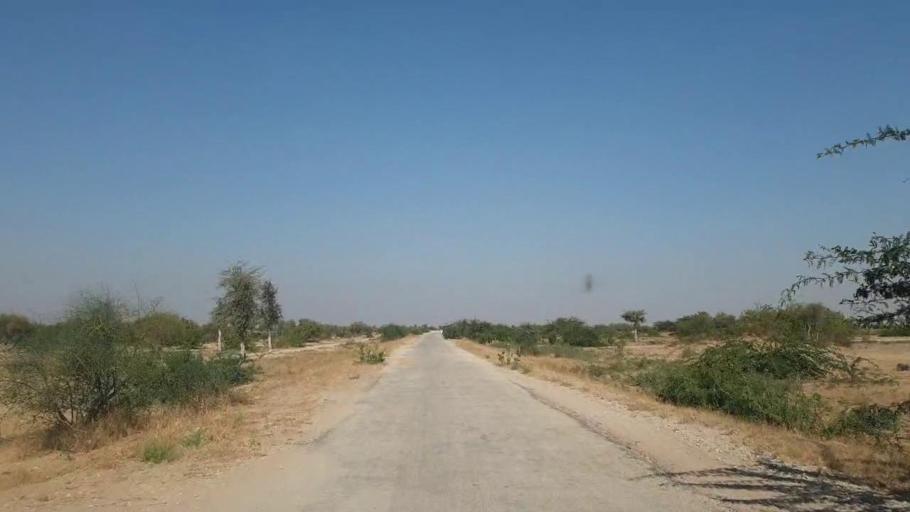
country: PK
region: Sindh
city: Jamshoro
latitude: 25.3799
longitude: 67.8438
